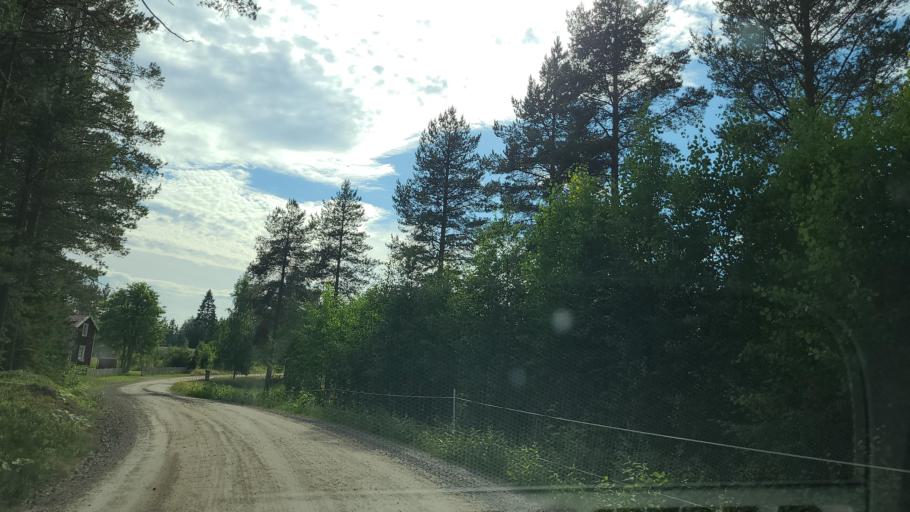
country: SE
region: Vaesterbotten
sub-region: Robertsfors Kommun
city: Robertsfors
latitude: 64.1576
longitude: 20.9336
